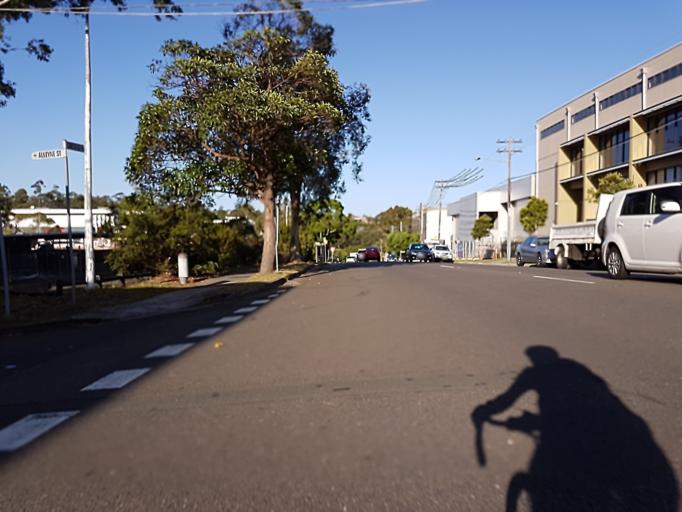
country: AU
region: New South Wales
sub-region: Ku-ring-gai
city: Roseville Chase
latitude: -33.7867
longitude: 151.1976
